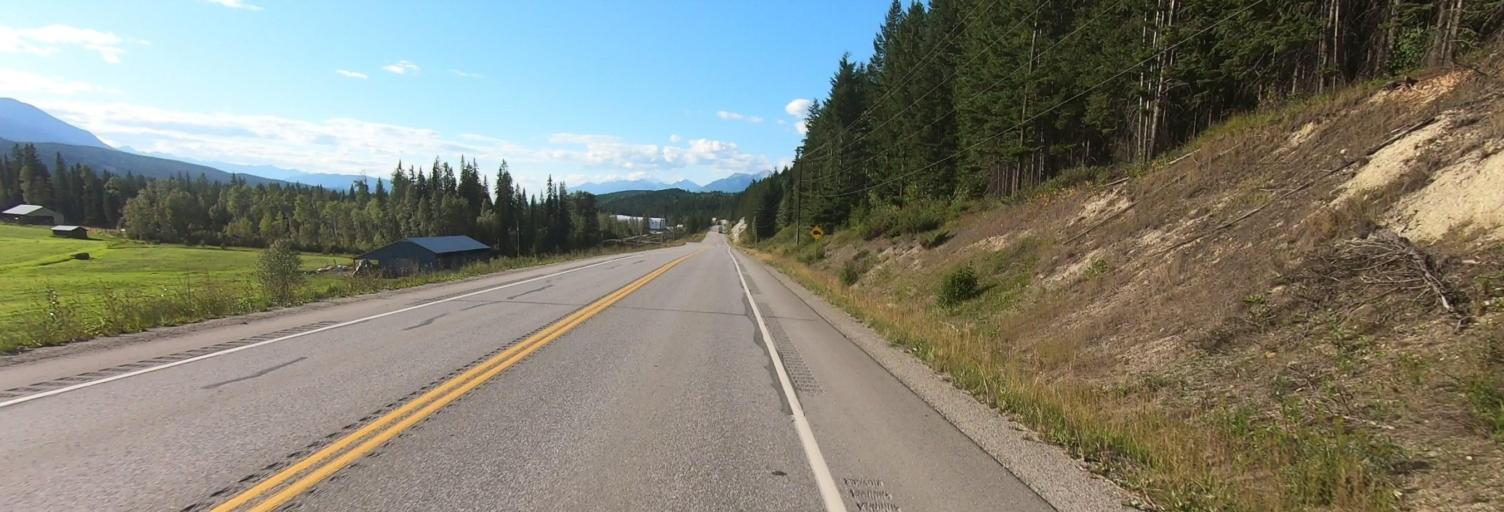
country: CA
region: British Columbia
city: Golden
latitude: 51.4189
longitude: -117.0527
